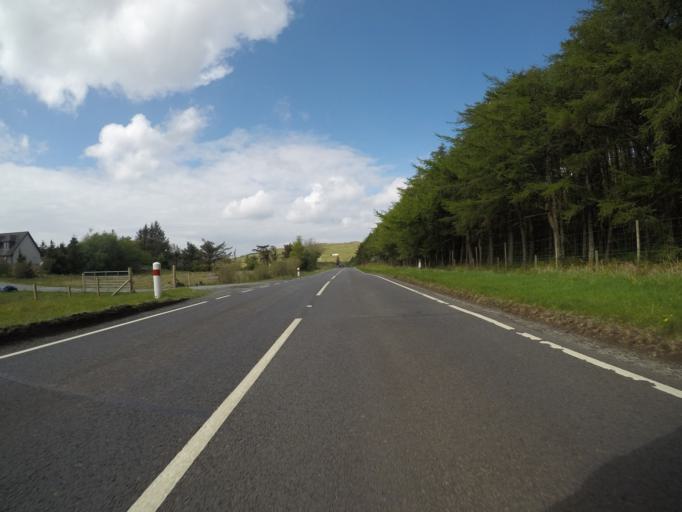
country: GB
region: Scotland
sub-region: Highland
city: Portree
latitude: 57.5282
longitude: -6.3481
